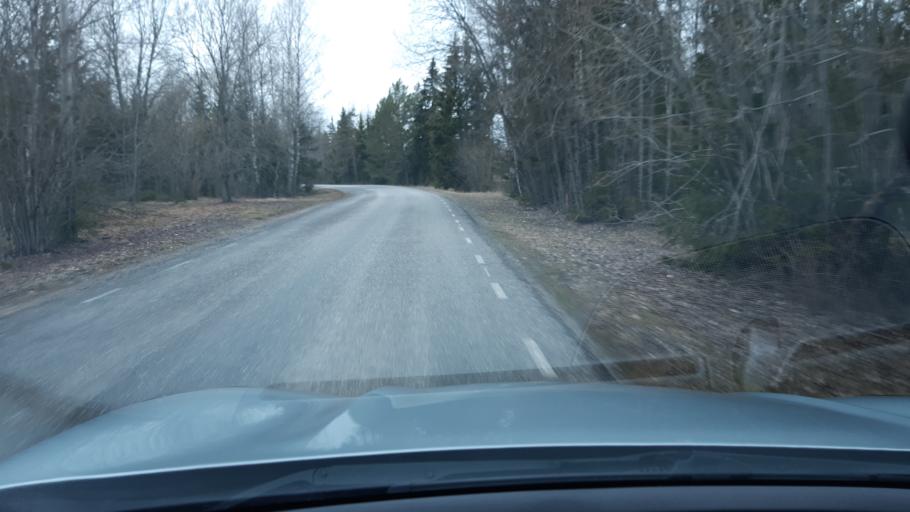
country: EE
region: Harju
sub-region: Saue linn
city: Saue
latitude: 59.1426
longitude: 24.5682
